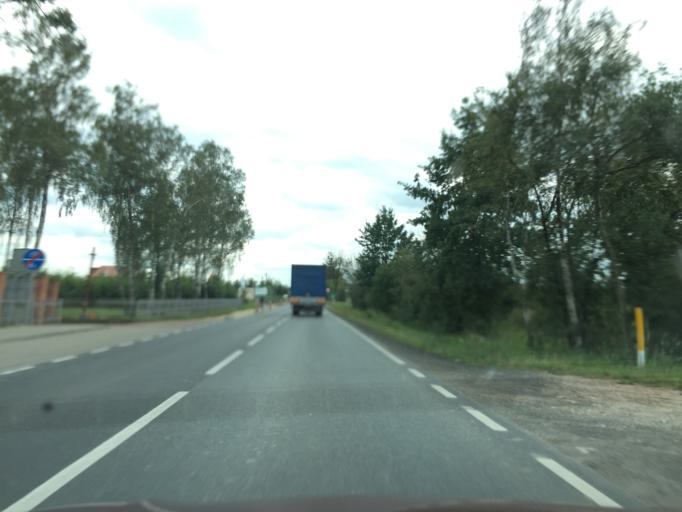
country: PL
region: Greater Poland Voivodeship
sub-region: Kalisz
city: Kalisz
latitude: 51.8050
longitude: 18.0928
